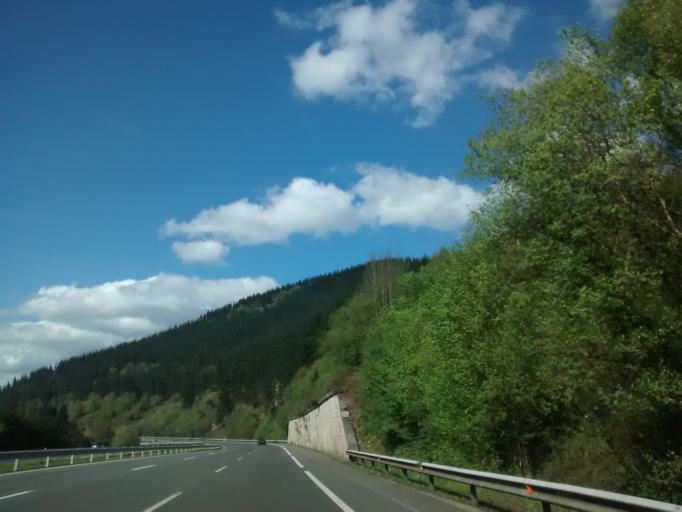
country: ES
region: Basque Country
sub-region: Bizkaia
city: Elexalde
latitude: 43.0812
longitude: -2.9153
